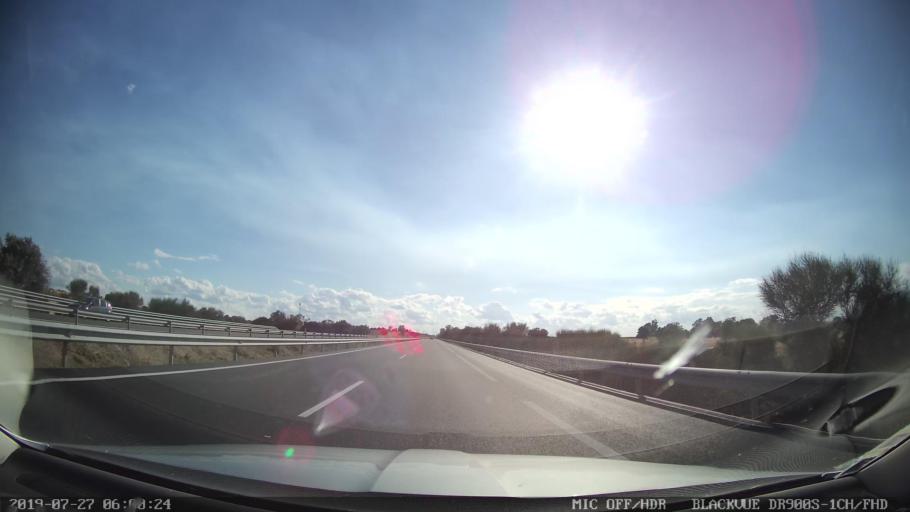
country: ES
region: Castille-La Mancha
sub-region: Province of Toledo
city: Caleruela
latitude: 39.8981
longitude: -5.2927
